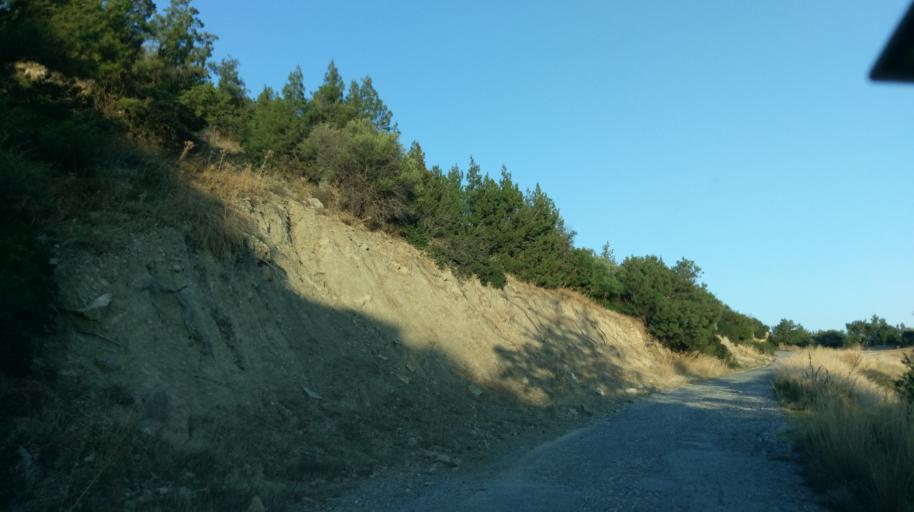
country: CY
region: Ammochostos
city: Trikomo
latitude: 35.3766
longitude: 33.9001
